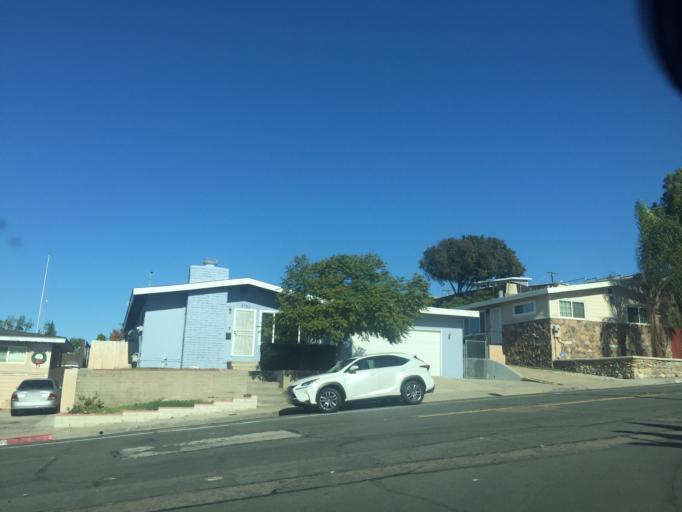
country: US
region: California
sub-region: San Diego County
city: La Mesa
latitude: 32.7848
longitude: -117.0925
